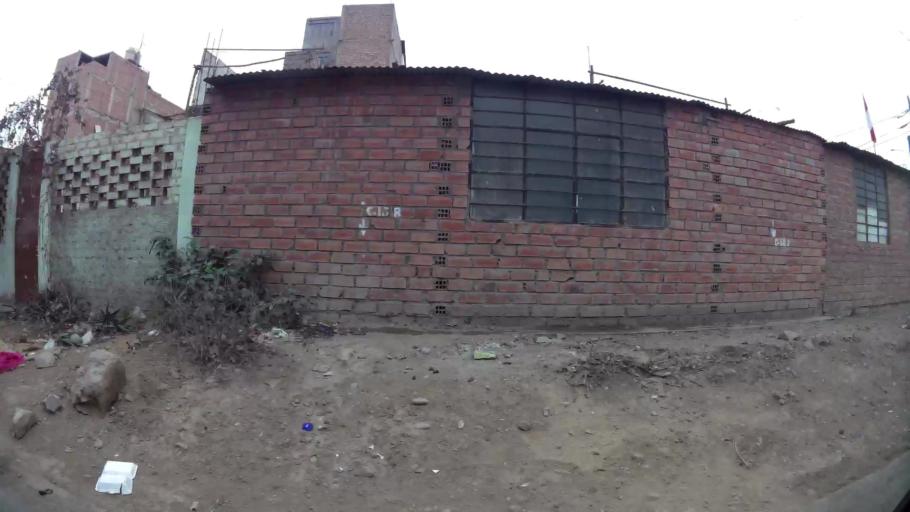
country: PE
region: Lima
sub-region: Lima
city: Independencia
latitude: -11.9430
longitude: -77.0855
